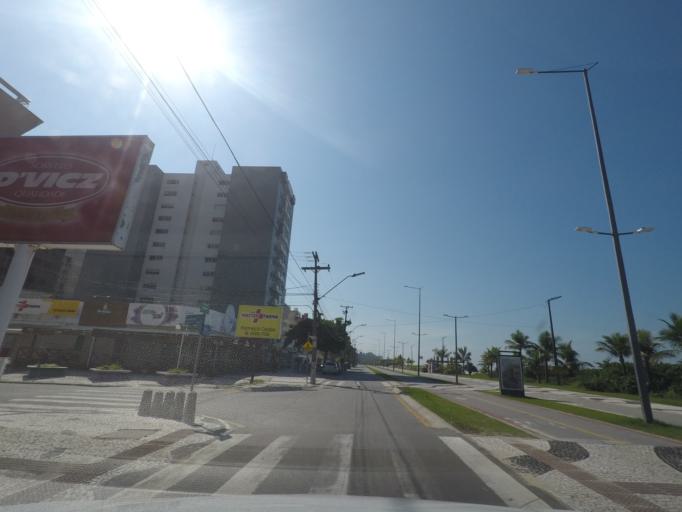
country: BR
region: Parana
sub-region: Guaratuba
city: Guaratuba
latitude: -25.8373
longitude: -48.5380
